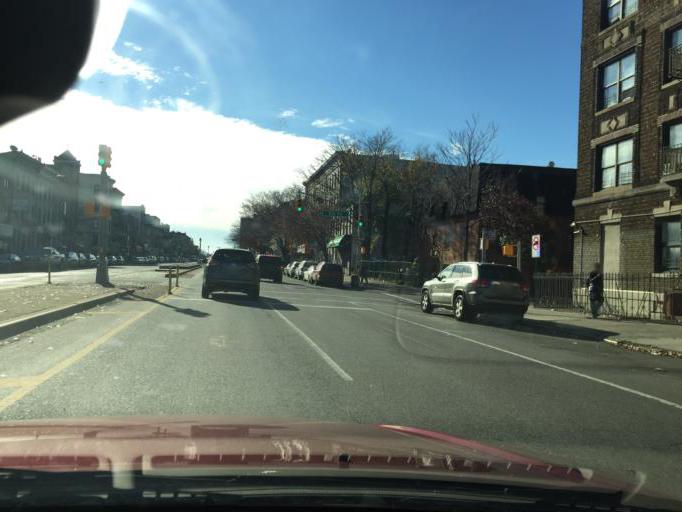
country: US
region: New York
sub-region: Kings County
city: Bensonhurst
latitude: 40.6440
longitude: -74.0153
